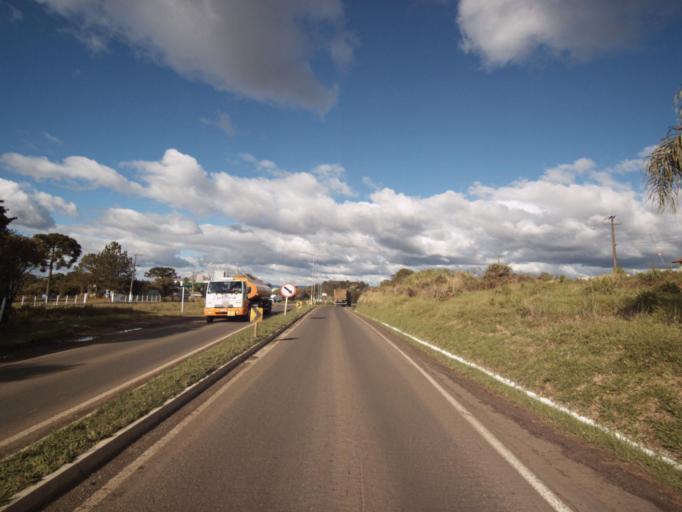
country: BR
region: Santa Catarina
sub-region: Joacaba
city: Joacaba
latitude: -27.1781
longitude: -51.5435
